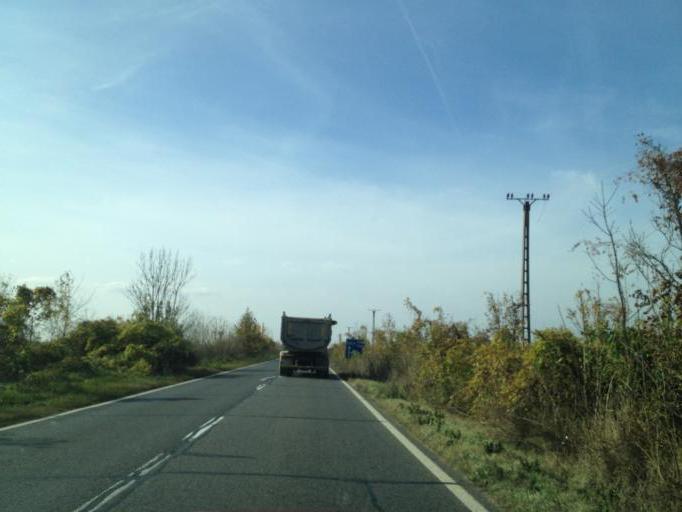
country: RO
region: Timis
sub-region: Comuna Faget
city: Faget
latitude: 45.8586
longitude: 22.2084
